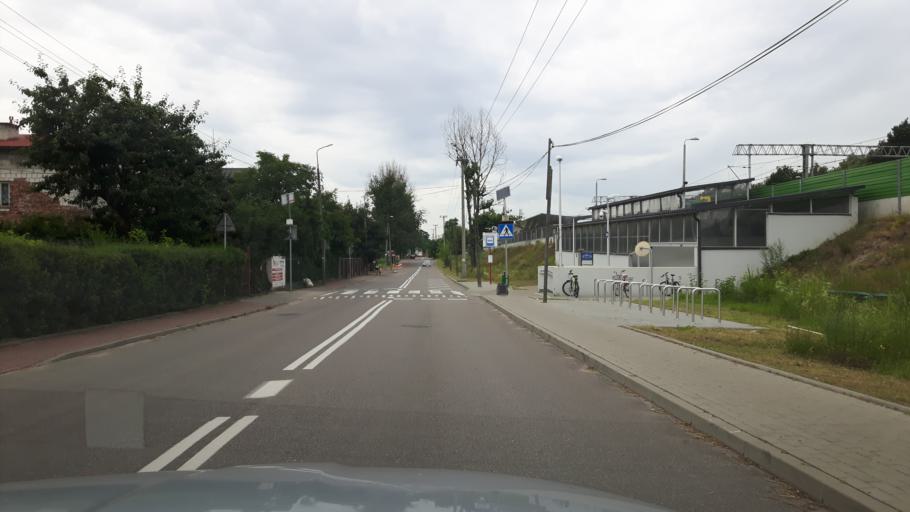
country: PL
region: Masovian Voivodeship
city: Zielonka
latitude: 52.3122
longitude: 21.1595
